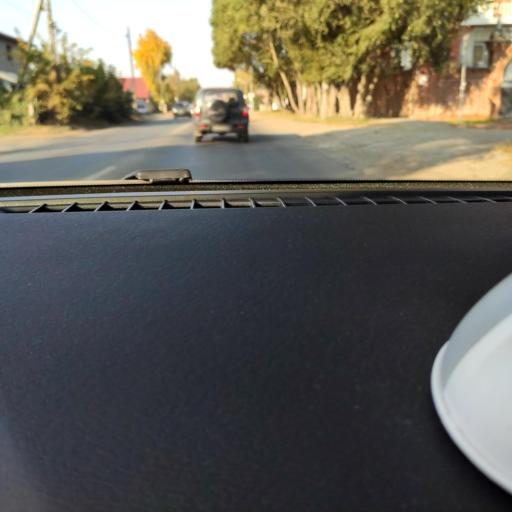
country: RU
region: Samara
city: Petra-Dubrava
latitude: 53.2533
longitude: 50.3191
